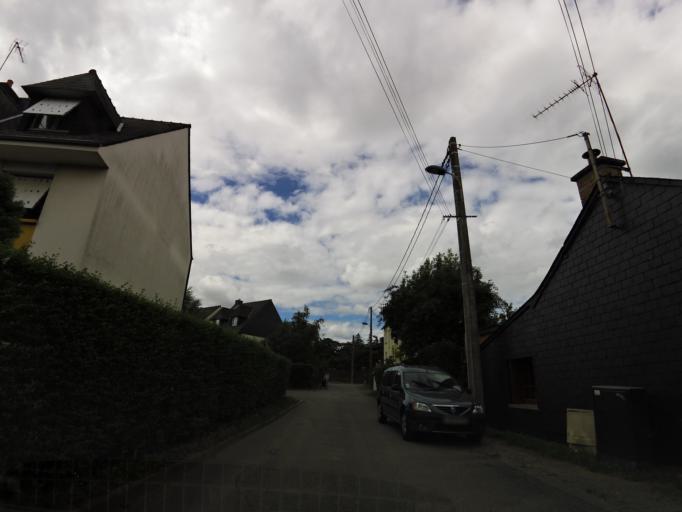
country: FR
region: Brittany
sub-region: Departement d'Ille-et-Vilaine
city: Rennes
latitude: 48.1235
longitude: -1.6785
